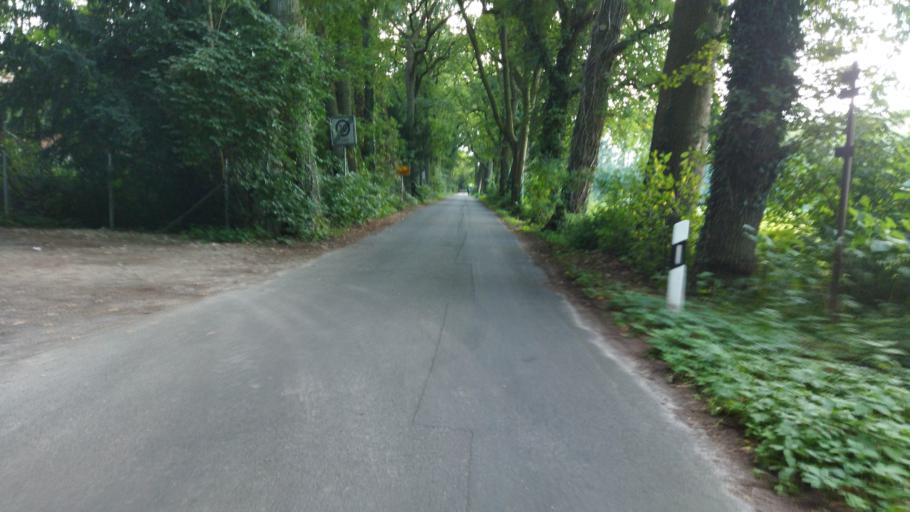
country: DE
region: Lower Saxony
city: Georgsmarienhutte
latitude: 52.2349
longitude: 8.0144
